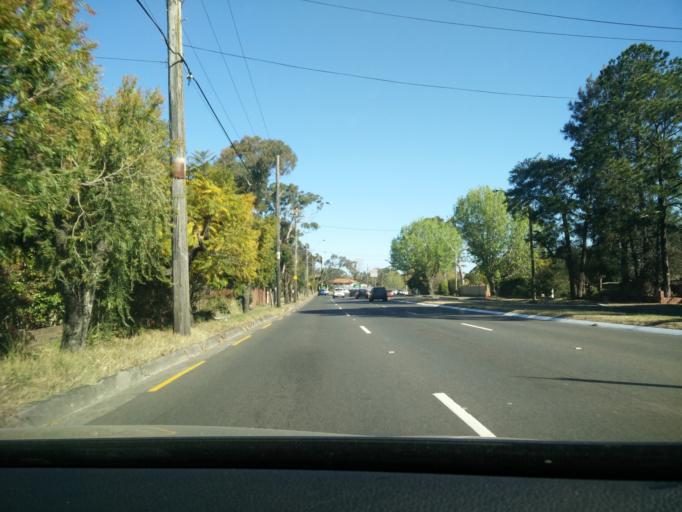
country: AU
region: New South Wales
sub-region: City of Sydney
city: Pymble
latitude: -33.7658
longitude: 151.1369
